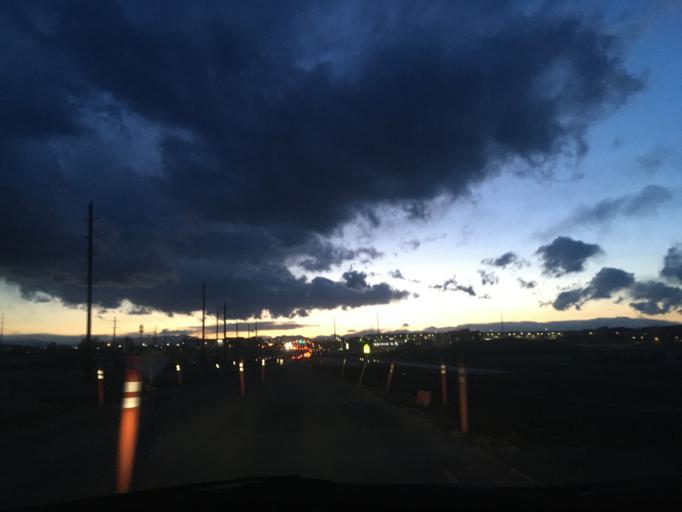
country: US
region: Colorado
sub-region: Adams County
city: Northglenn
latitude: 39.9575
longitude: -104.9721
